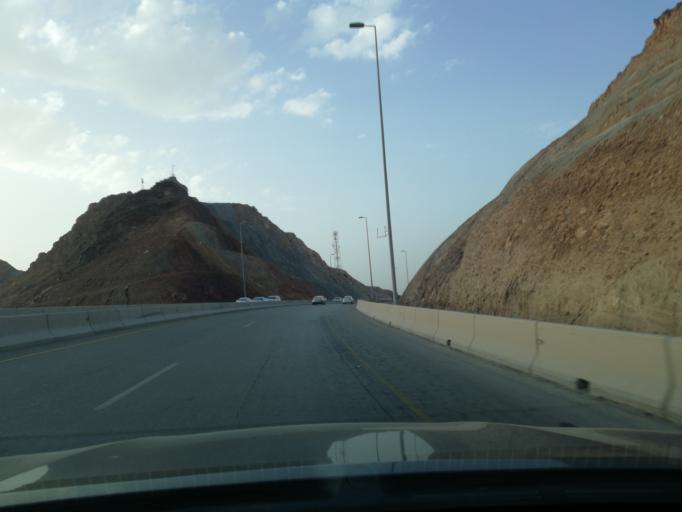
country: OM
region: Muhafazat ad Dakhiliyah
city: Bidbid
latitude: 23.4558
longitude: 58.1169
